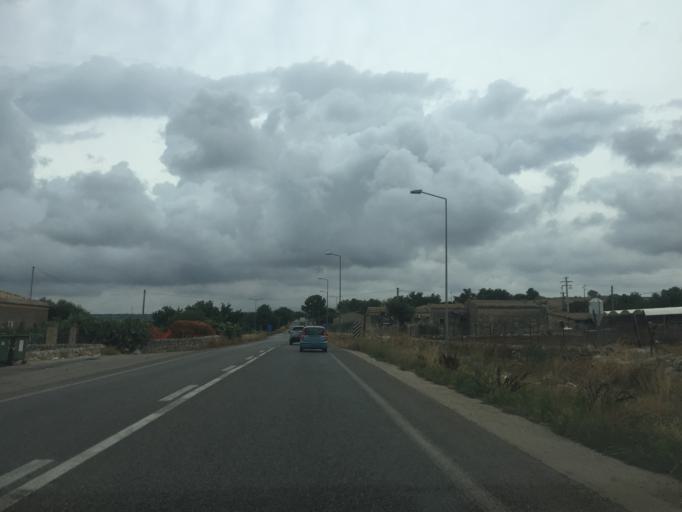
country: IT
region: Sicily
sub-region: Ragusa
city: Marina di Ragusa
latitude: 36.8284
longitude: 14.5845
